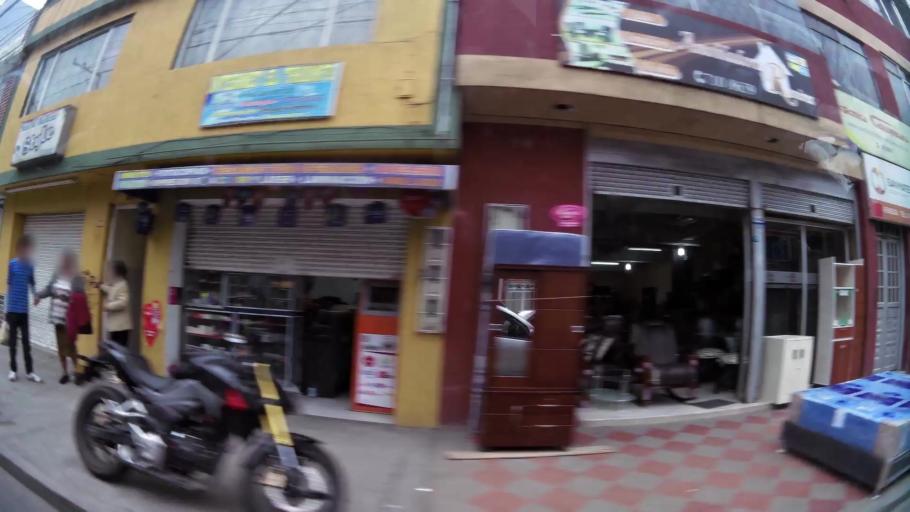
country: CO
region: Bogota D.C.
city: Bogota
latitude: 4.5947
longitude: -74.1396
